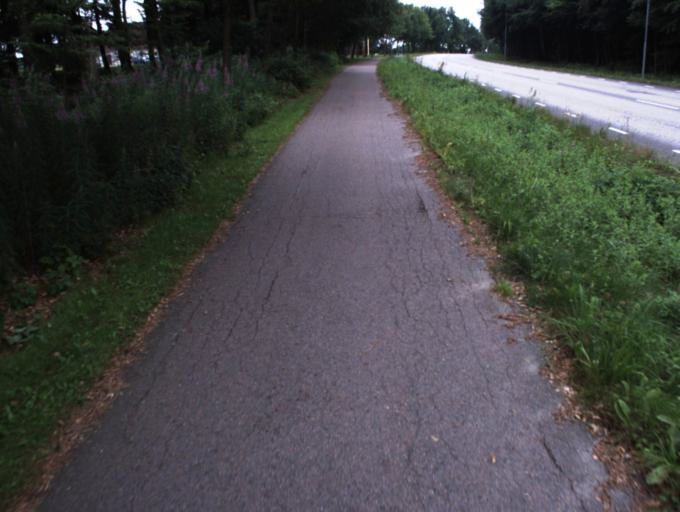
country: SE
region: Skane
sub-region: Helsingborg
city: Odakra
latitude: 56.0871
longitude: 12.7431
